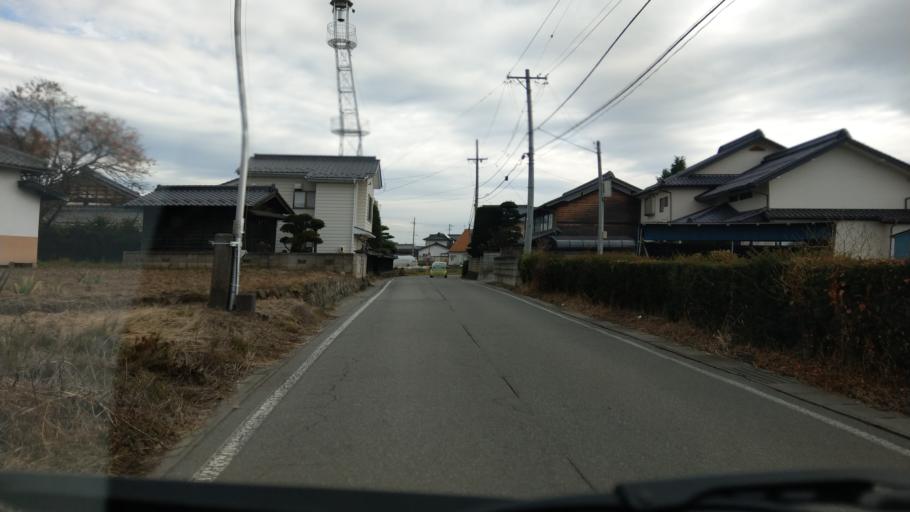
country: JP
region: Nagano
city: Komoro
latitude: 36.3221
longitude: 138.4606
